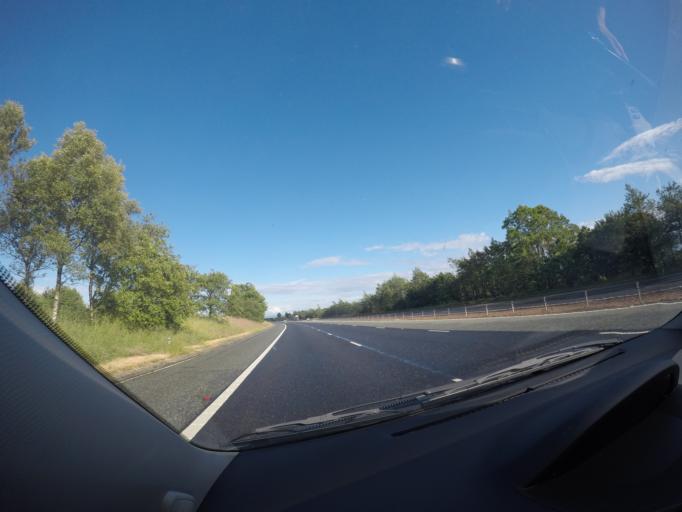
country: GB
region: Scotland
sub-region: Dumfries and Galloway
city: Annan
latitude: 55.0321
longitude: -3.1666
